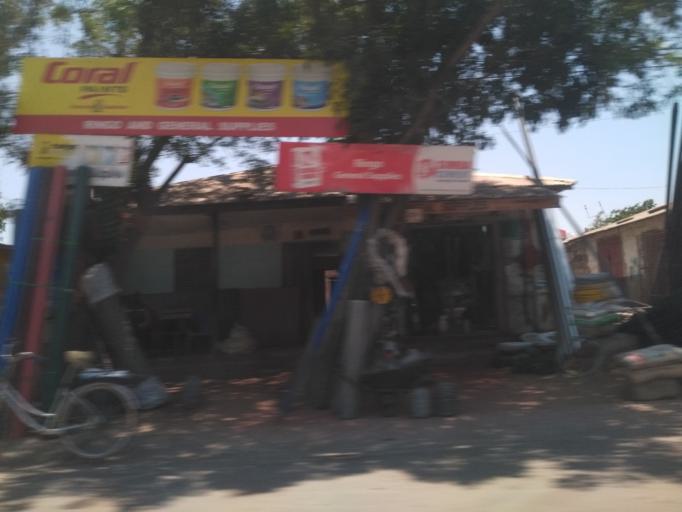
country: TZ
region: Dodoma
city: Dodoma
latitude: -6.1748
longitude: 35.7418
